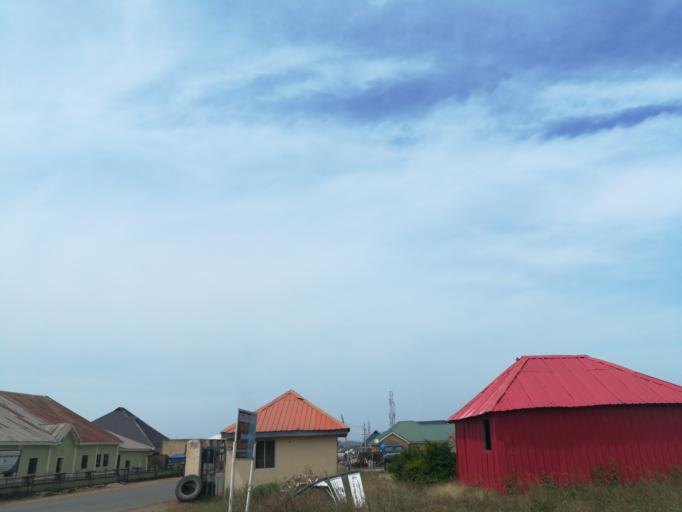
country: NG
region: Plateau
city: Jos
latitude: 9.8791
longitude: 8.8510
